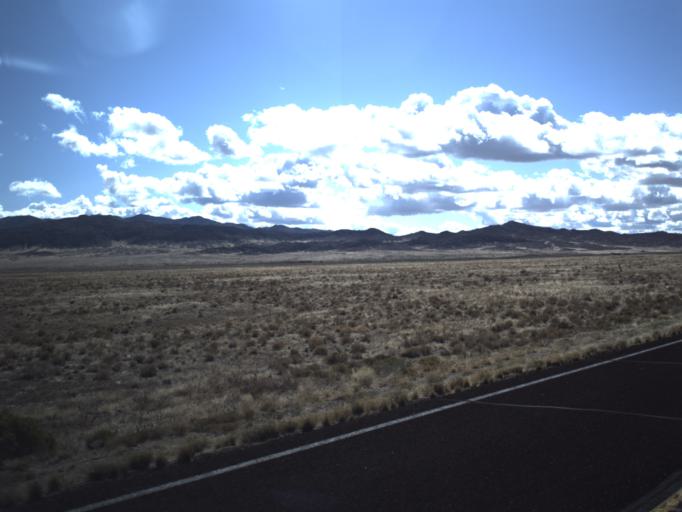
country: US
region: Nevada
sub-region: White Pine County
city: McGill
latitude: 38.9759
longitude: -114.0341
